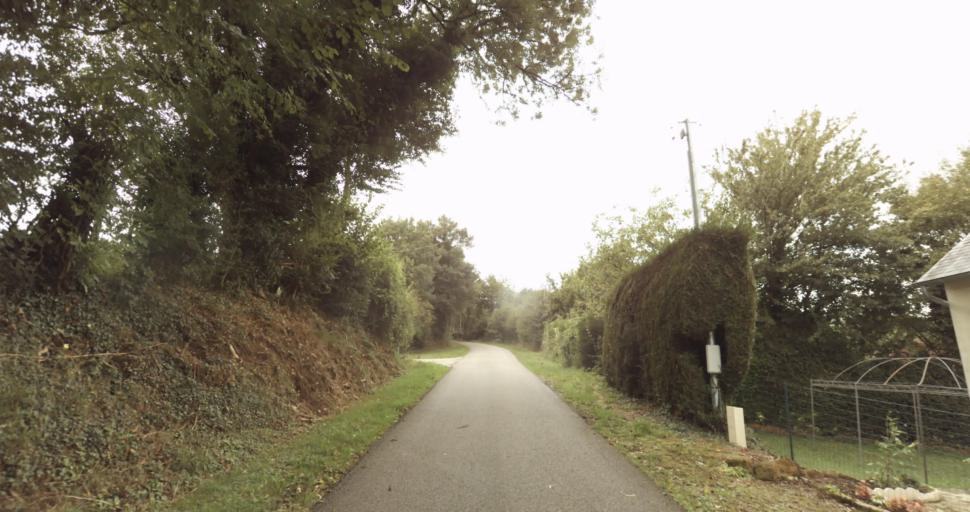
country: FR
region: Lower Normandy
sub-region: Departement de l'Orne
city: Gace
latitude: 48.8090
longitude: 0.2846
